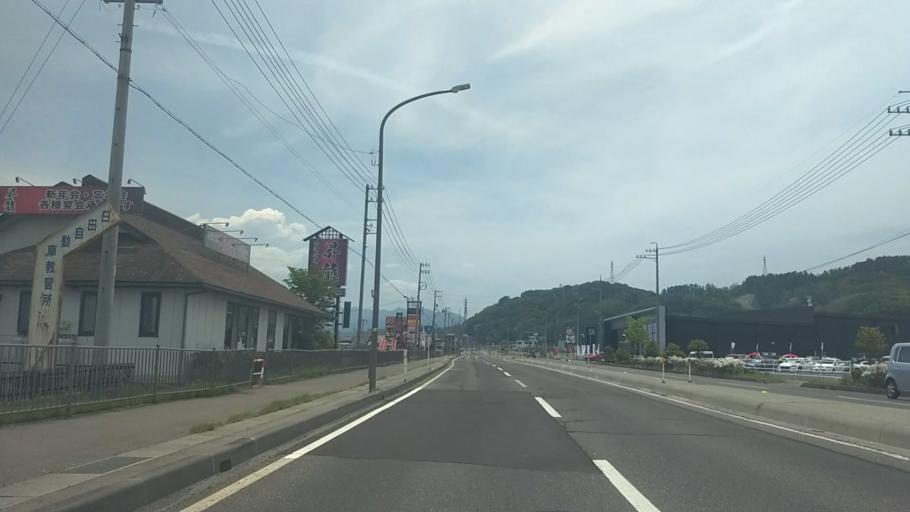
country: JP
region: Nagano
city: Saku
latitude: 36.2087
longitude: 138.4664
